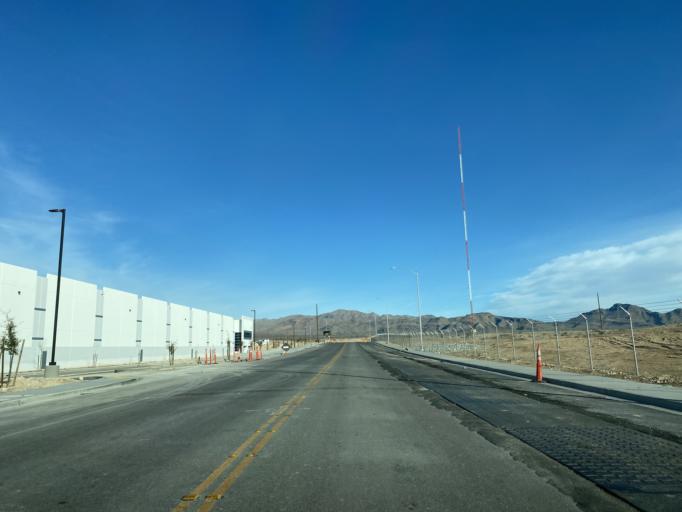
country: US
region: Nevada
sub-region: Clark County
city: Nellis Air Force Base
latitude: 36.2675
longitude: -115.0476
